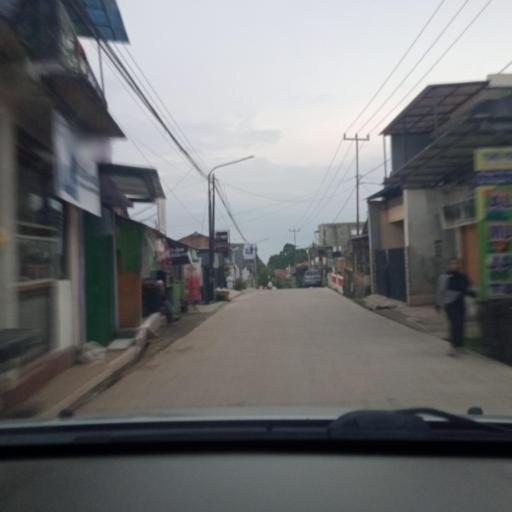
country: ID
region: West Java
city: Lembang
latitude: -6.8346
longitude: 107.5858
